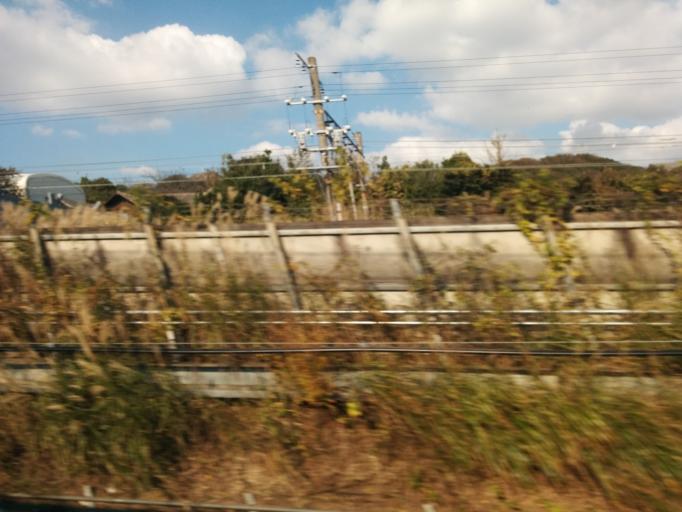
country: JP
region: Aichi
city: Toyohashi
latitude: 34.7283
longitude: 137.4276
